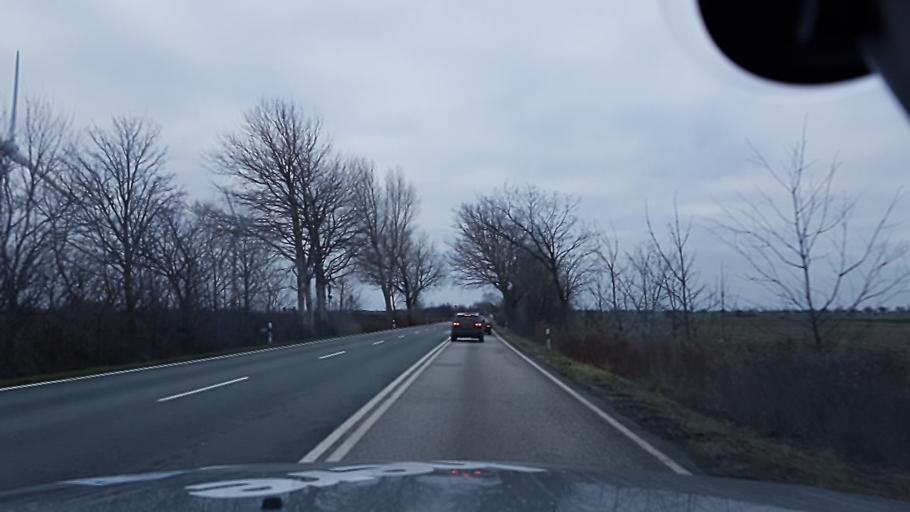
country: DE
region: Schleswig-Holstein
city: Fehmarn
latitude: 54.4888
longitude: 11.2177
